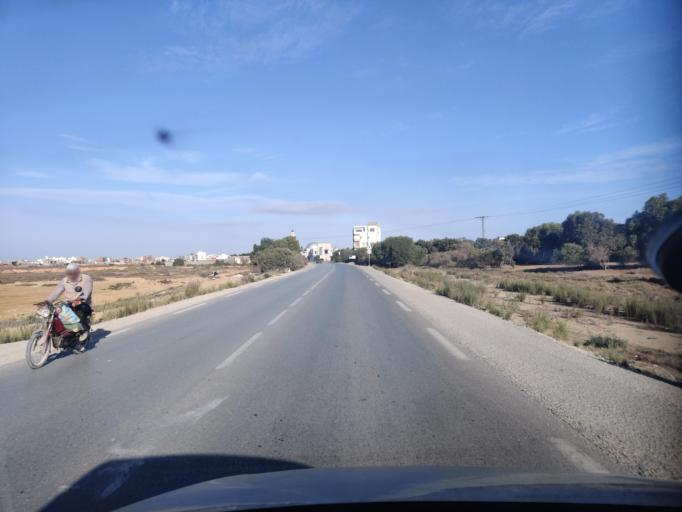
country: TN
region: Ariana
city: Ariana
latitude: 36.9527
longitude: 10.2339
